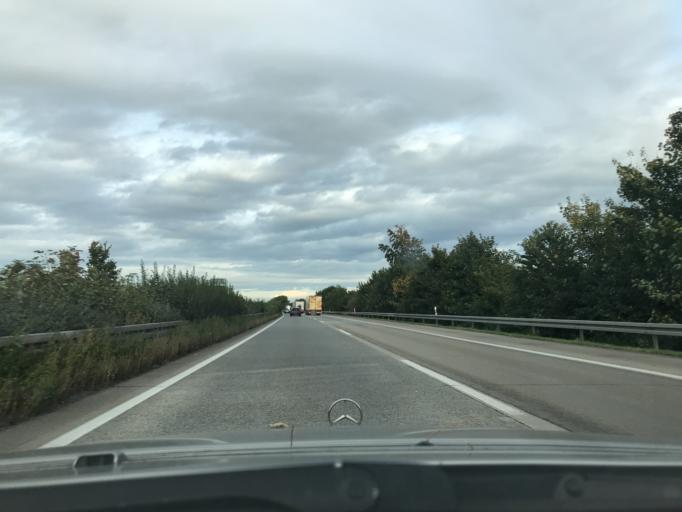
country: DE
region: North Rhine-Westphalia
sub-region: Regierungsbezirk Arnsberg
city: Bad Sassendorf
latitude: 51.5575
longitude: 8.1790
